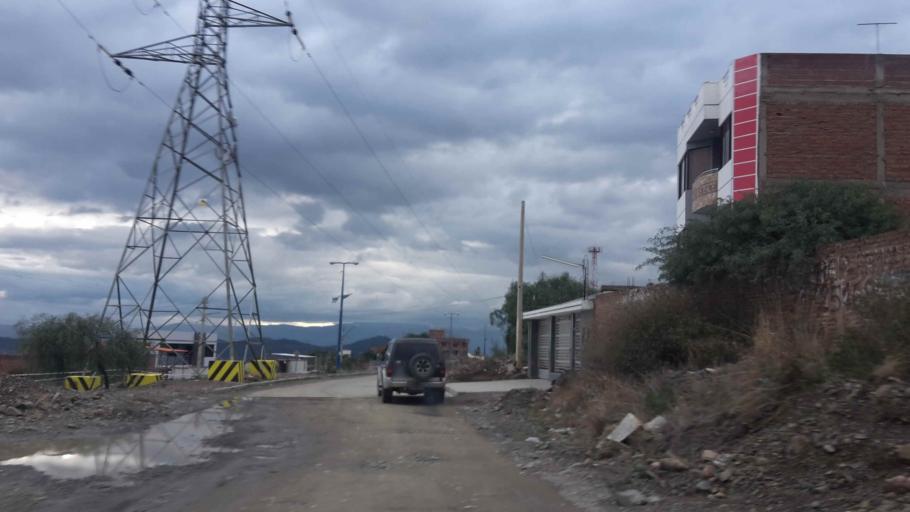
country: BO
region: Cochabamba
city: Cochabamba
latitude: -17.3791
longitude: -66.0707
